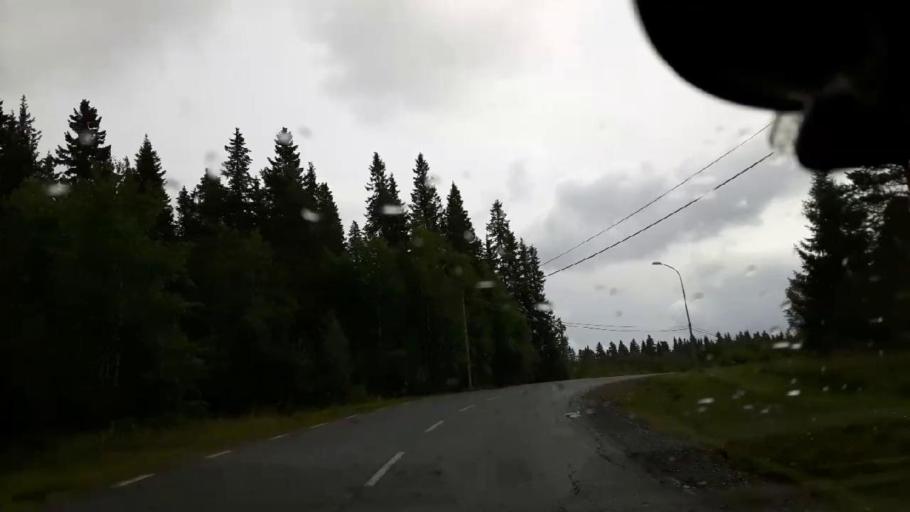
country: SE
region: Jaemtland
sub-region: Krokoms Kommun
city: Valla
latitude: 63.4094
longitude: 13.8140
